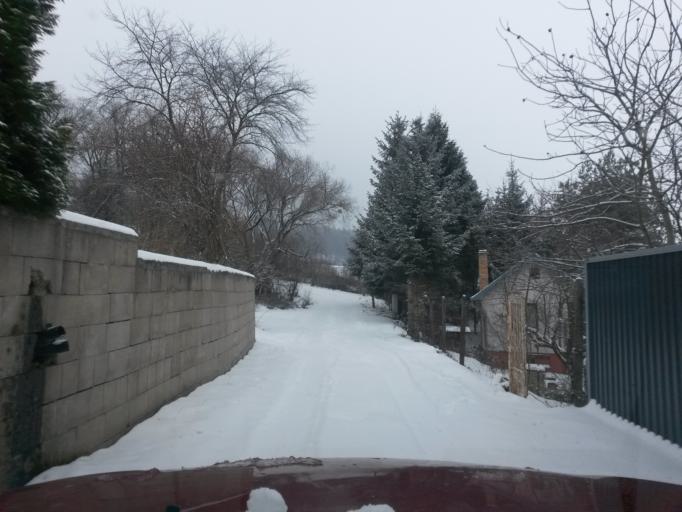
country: SK
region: Kosicky
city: Kosice
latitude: 48.7247
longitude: 21.3275
